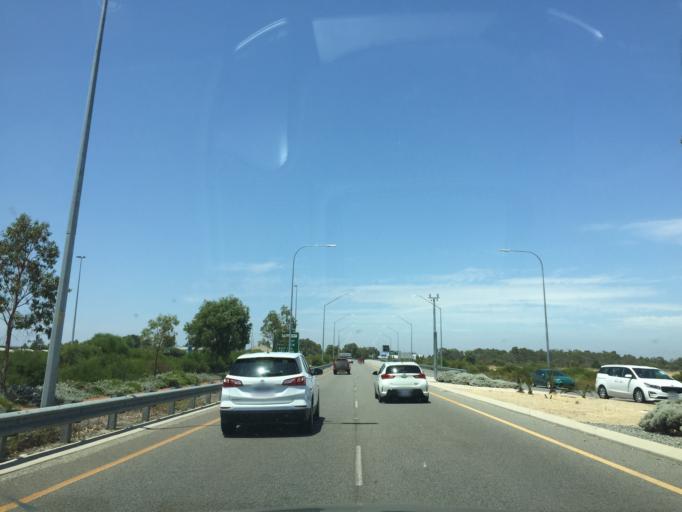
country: AU
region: Western Australia
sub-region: Belmont
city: Kewdale
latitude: -31.9564
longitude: 115.9689
